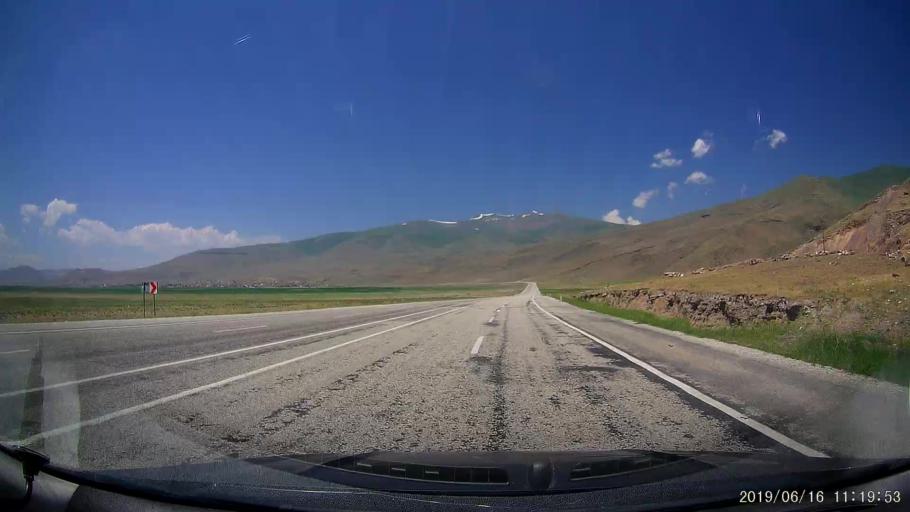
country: TR
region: Agri
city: Dogubayazit
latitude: 39.6958
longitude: 44.1043
